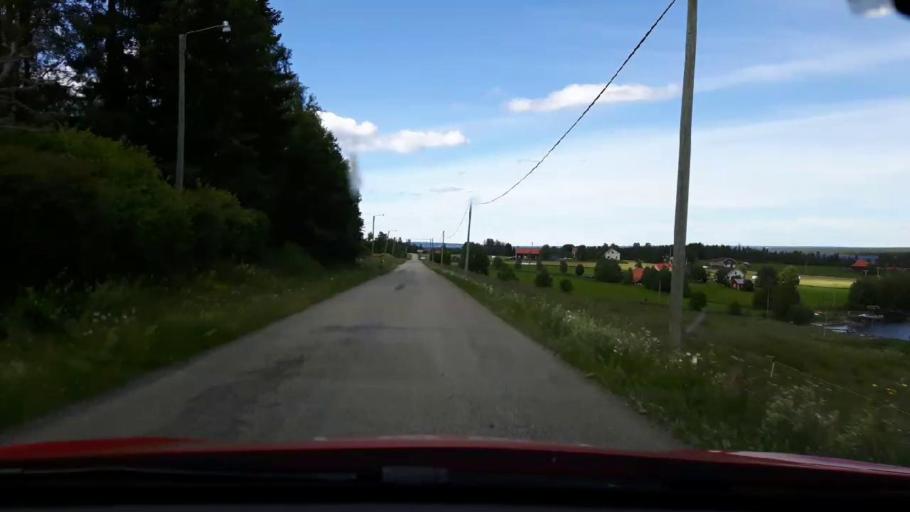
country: SE
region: Jaemtland
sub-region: Bergs Kommun
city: Hoverberg
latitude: 62.8254
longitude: 14.4603
